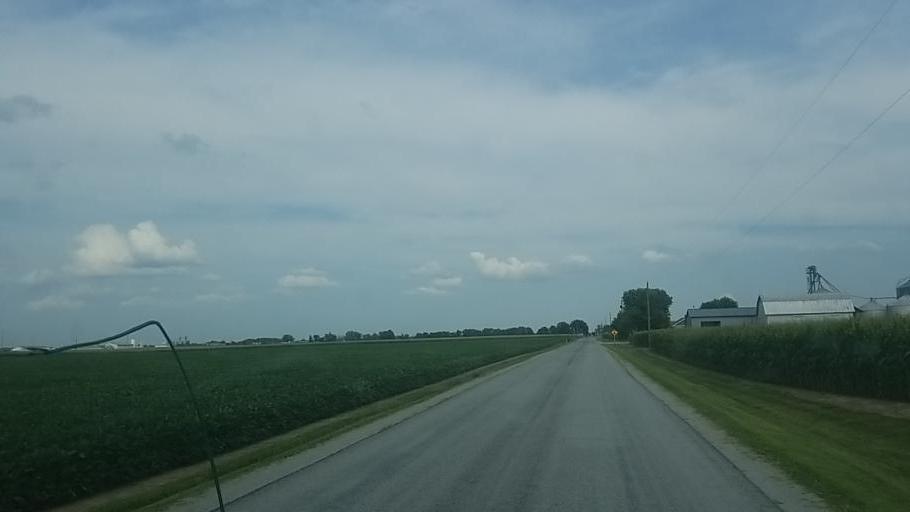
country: US
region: Ohio
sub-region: Wyandot County
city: Upper Sandusky
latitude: 40.8179
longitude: -83.3282
